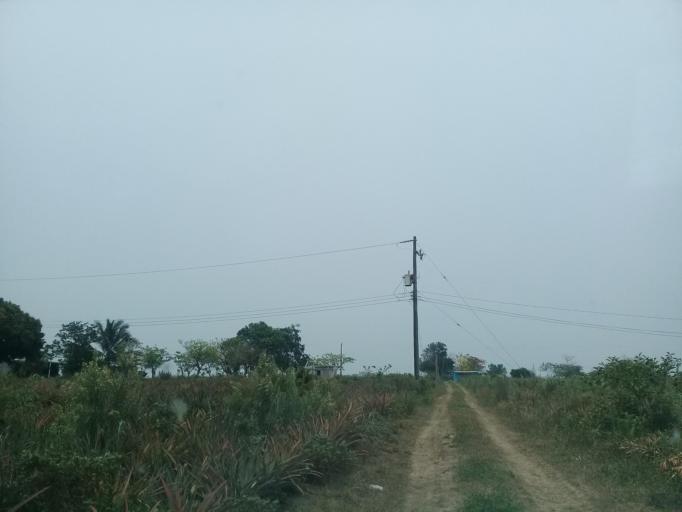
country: MX
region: Veracruz
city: Paso del Toro
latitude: 18.9738
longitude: -96.1390
